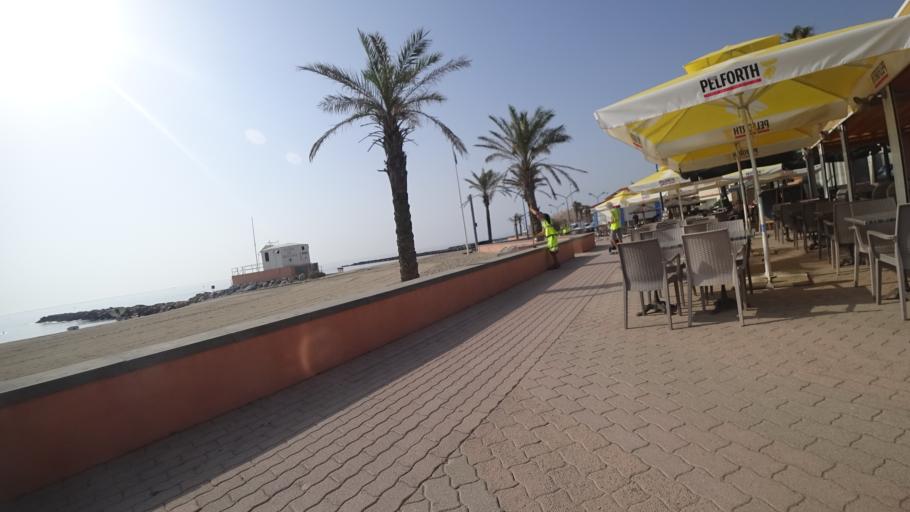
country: FR
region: Languedoc-Roussillon
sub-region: Departement des Pyrenees-Orientales
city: Sainte-Marie-Plage
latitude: 42.7285
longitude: 3.0383
